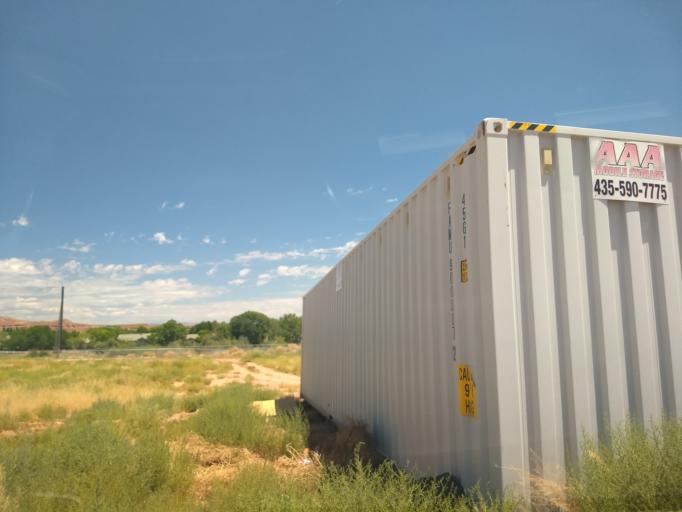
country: US
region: Utah
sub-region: Washington County
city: Washington
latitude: 37.1314
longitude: -113.5252
